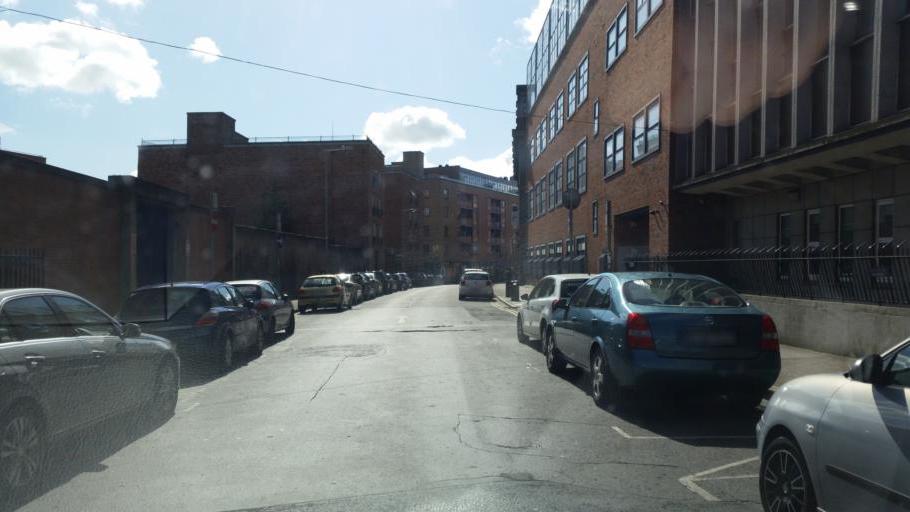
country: IE
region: Leinster
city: Drumcondra
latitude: 53.3519
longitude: -6.2686
